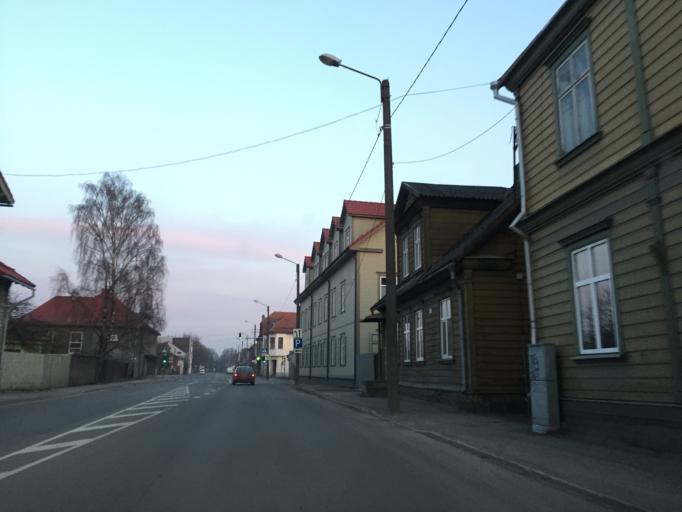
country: EE
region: Paernumaa
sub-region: Paernu linn
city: Parnu
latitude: 58.3857
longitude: 24.5123
